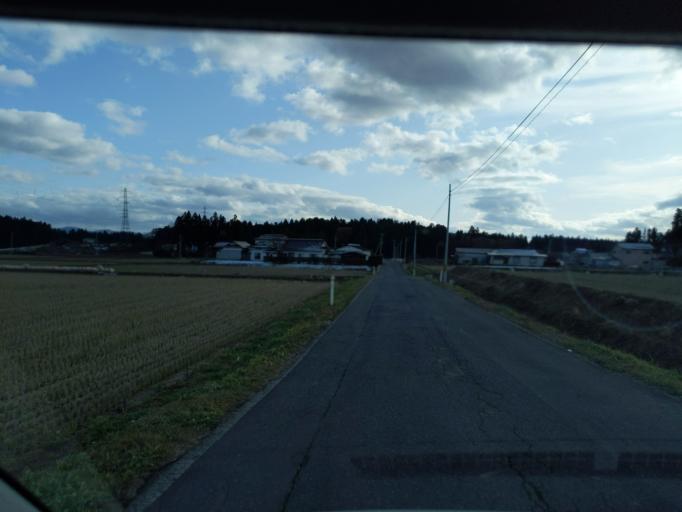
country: JP
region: Iwate
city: Mizusawa
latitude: 39.1193
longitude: 141.0821
